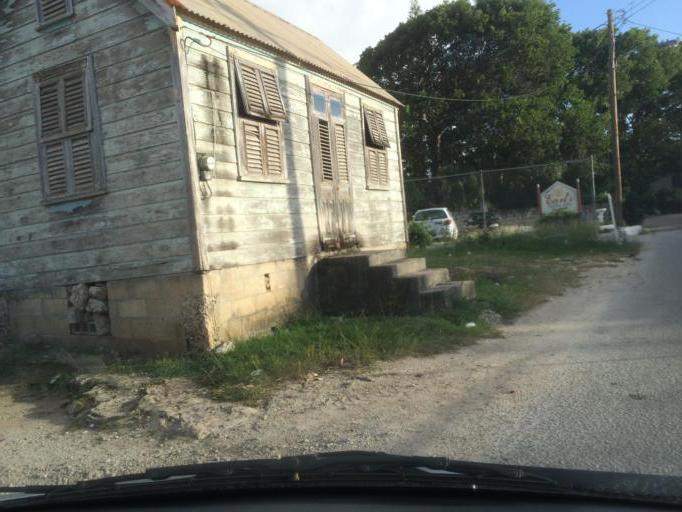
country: BB
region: Saint Lucy
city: Checker Hall
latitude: 13.2770
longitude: -59.6471
